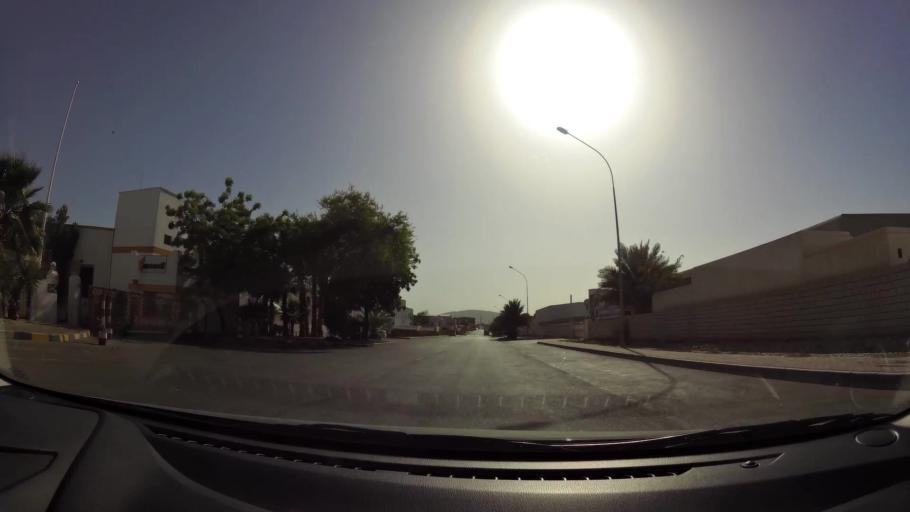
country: OM
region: Muhafazat Masqat
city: As Sib al Jadidah
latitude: 23.5520
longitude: 58.2216
